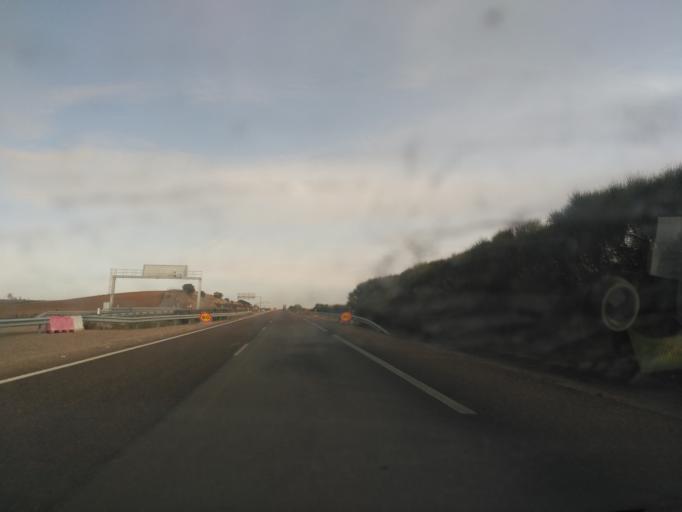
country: ES
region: Castille and Leon
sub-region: Provincia de Salamanca
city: Cabrerizos
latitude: 41.0023
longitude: -5.6131
